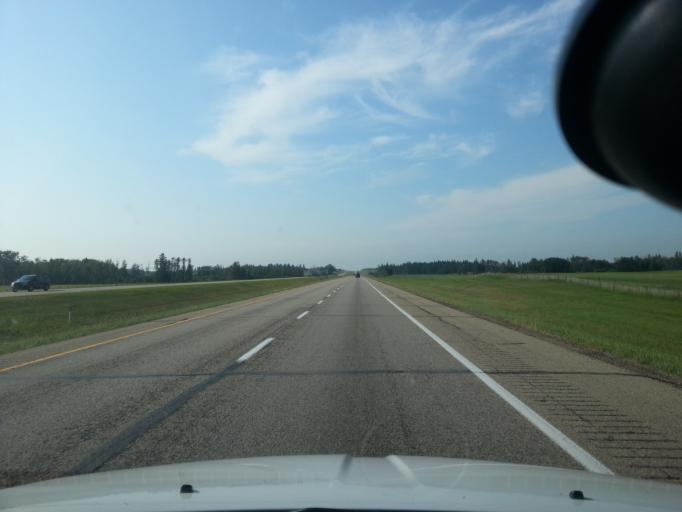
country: CA
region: Alberta
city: Ponoka
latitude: 52.6284
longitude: -113.6638
